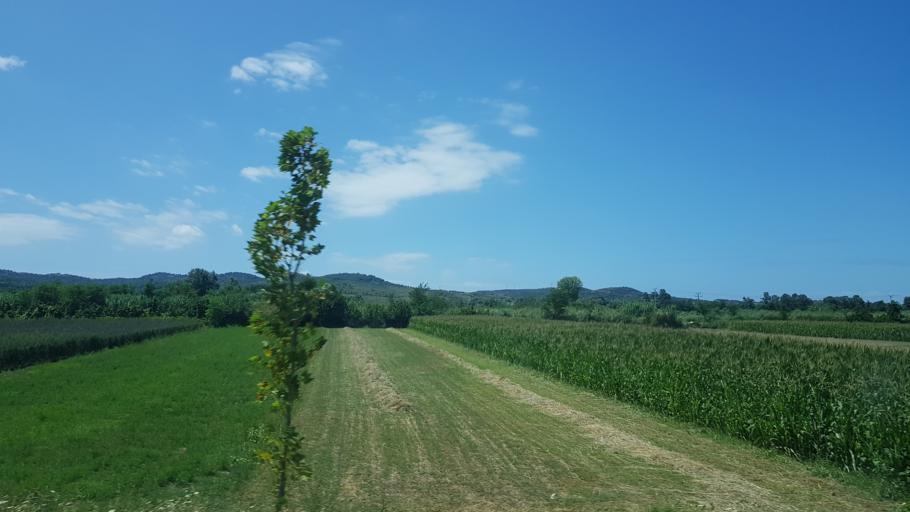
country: AL
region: Fier
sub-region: Rrethi i Fierit
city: Frakulla e Madhe
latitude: 40.6127
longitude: 19.5239
